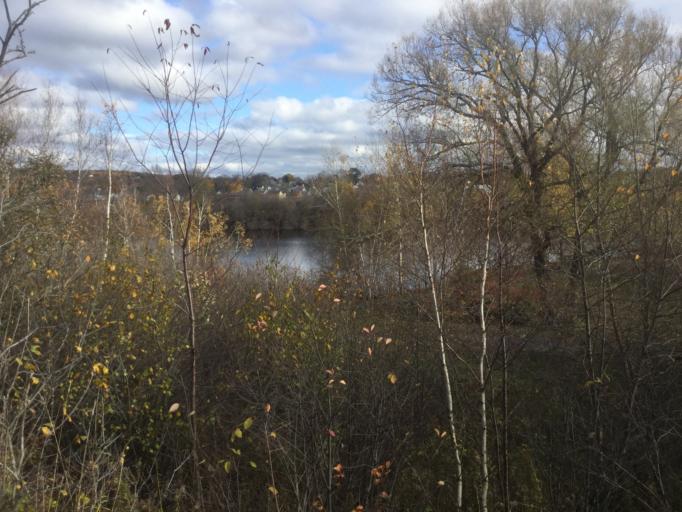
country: CA
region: Nova Scotia
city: New Glasgow
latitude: 45.5809
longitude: -62.6553
